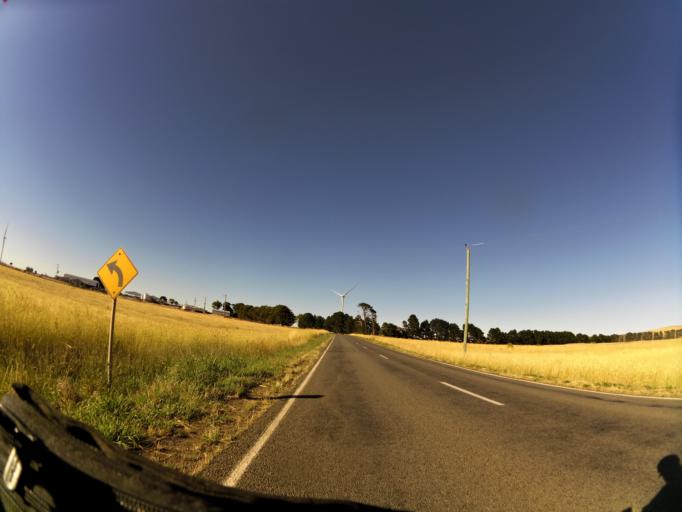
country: AU
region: Victoria
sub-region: Ballarat North
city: Delacombe
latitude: -37.5621
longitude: 143.3607
